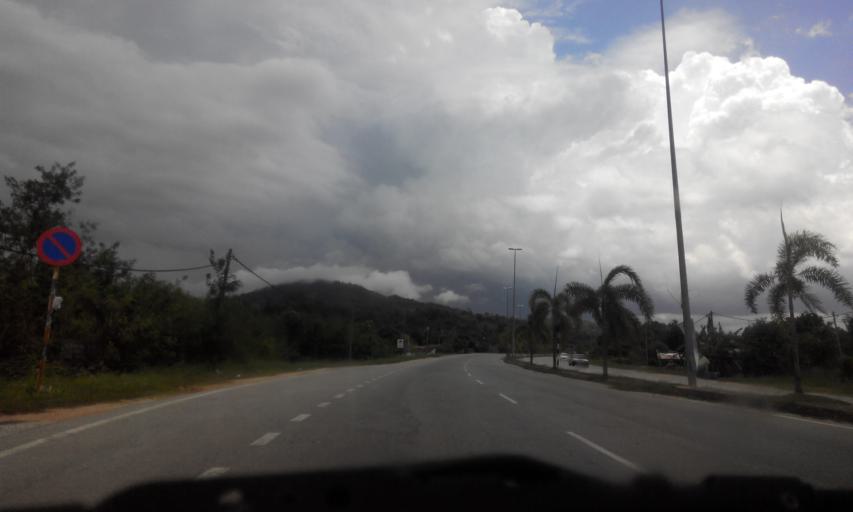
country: MY
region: Perak
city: Parit Buntar
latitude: 5.1280
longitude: 100.5083
